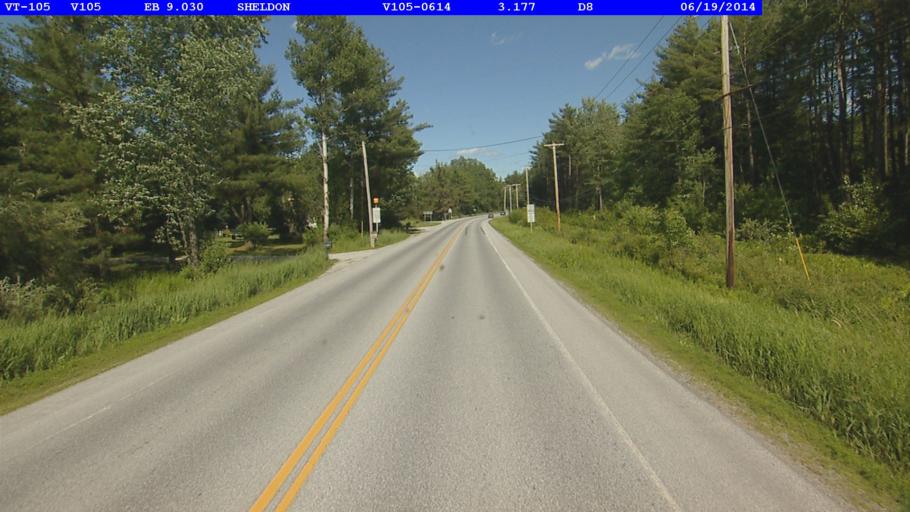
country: US
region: Vermont
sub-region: Franklin County
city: Saint Albans
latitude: 44.9024
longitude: -72.9691
